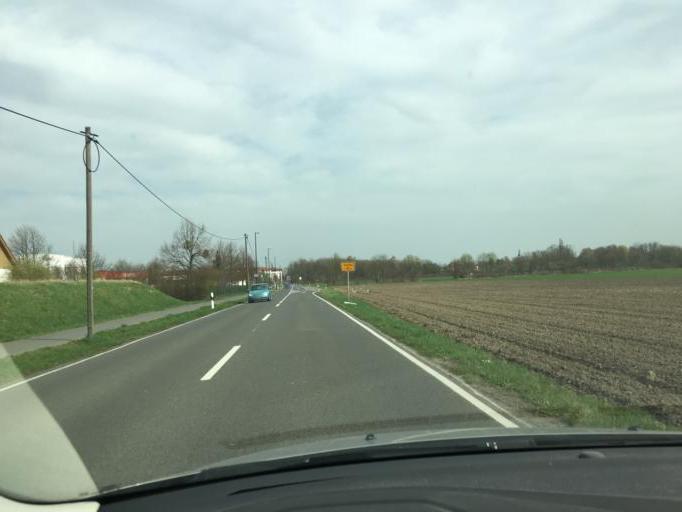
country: DE
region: Saxony
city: Taucha
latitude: 51.3697
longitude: 12.4928
